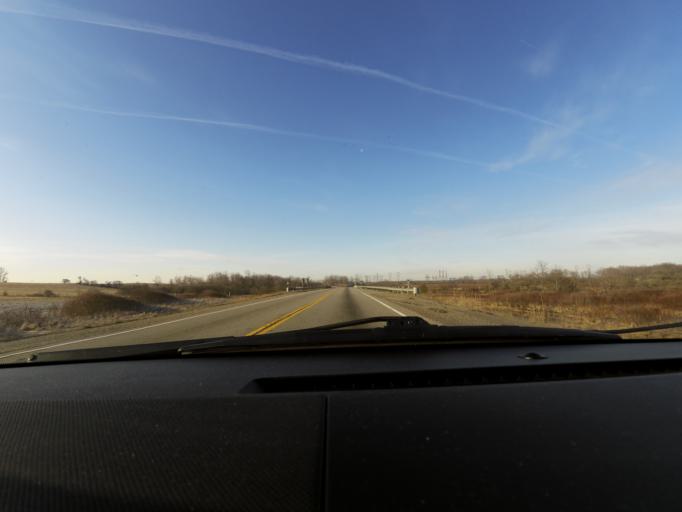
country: CA
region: Ontario
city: Ancaster
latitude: 43.0900
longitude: -79.9588
